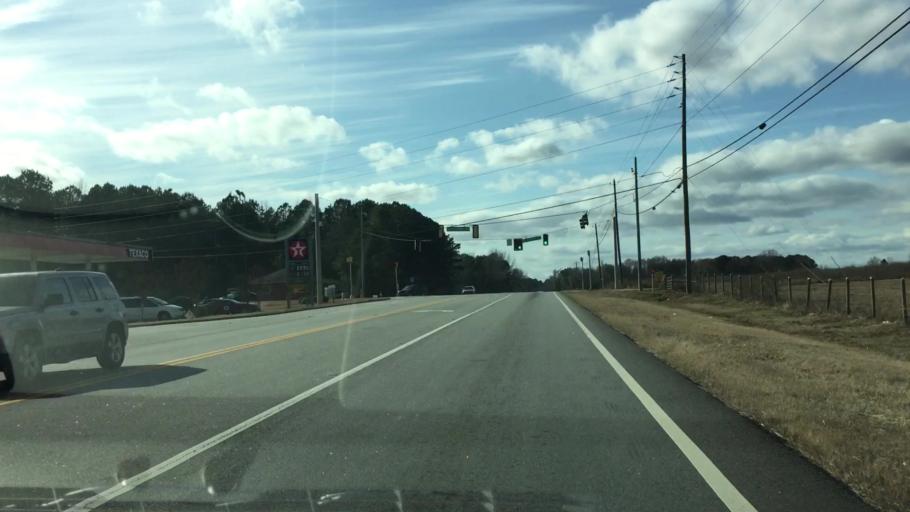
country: US
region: Georgia
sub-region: Henry County
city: McDonough
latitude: 33.4377
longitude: -84.0308
